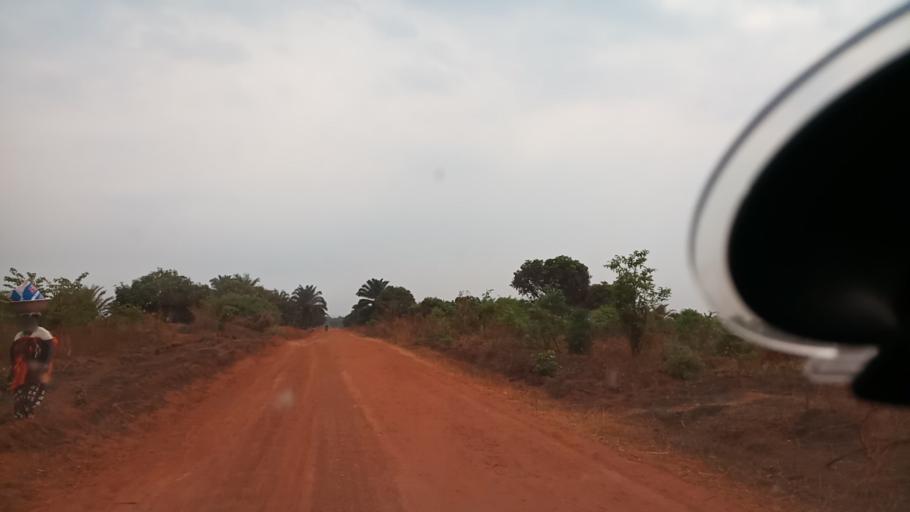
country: ZM
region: Luapula
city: Nchelenge
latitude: -9.1404
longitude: 28.2943
